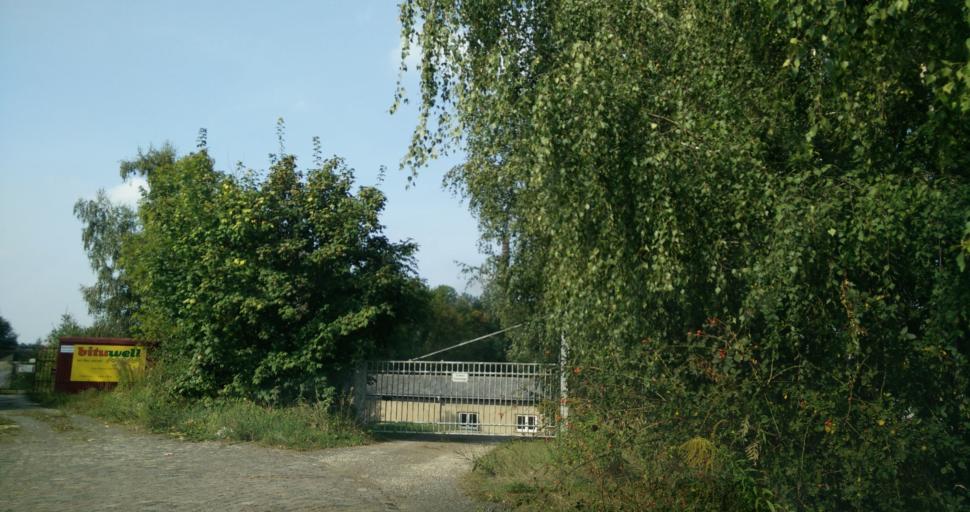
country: DE
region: Saxony
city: Colditz
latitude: 51.1440
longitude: 12.7931
